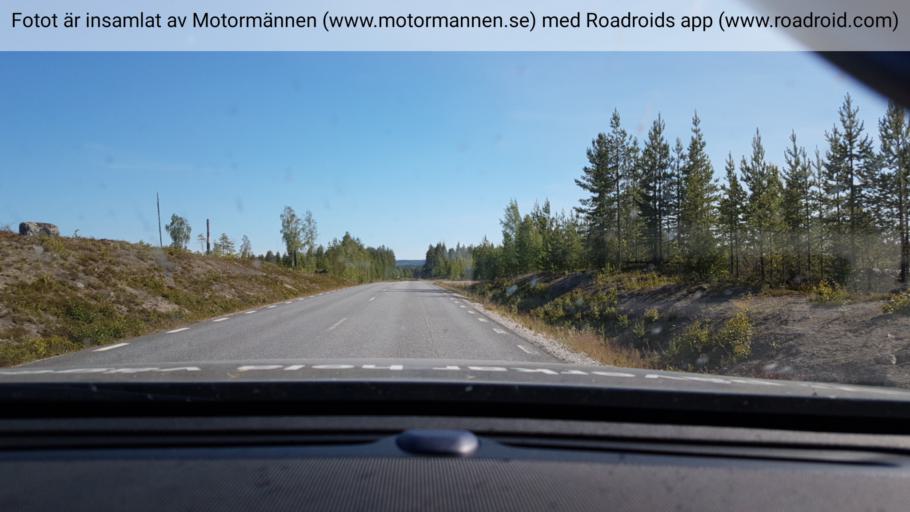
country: SE
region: Vaesterbotten
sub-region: Lycksele Kommun
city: Lycksele
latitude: 64.4976
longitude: 18.8978
